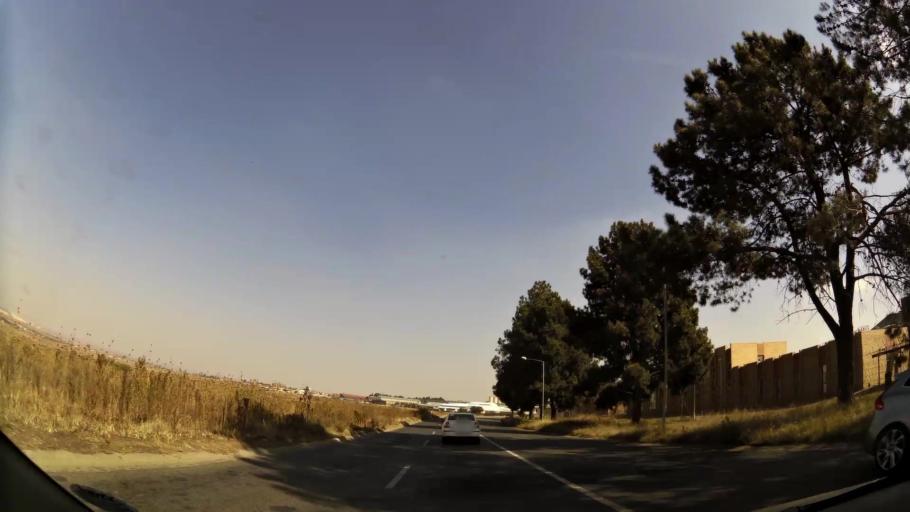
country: ZA
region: Gauteng
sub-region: City of Johannesburg Metropolitan Municipality
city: Roodepoort
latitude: -26.1545
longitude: 27.8085
